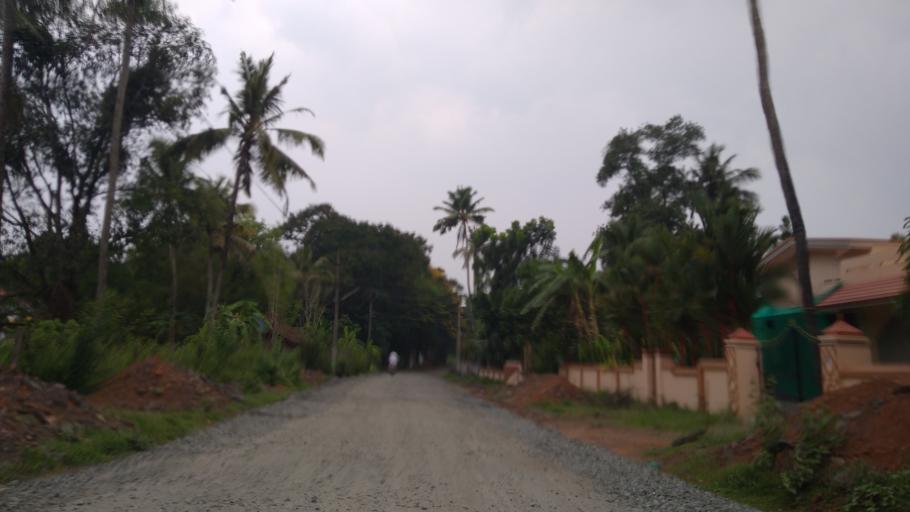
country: IN
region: Kerala
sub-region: Ernakulam
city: Perumbavoor
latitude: 10.0630
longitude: 76.5054
